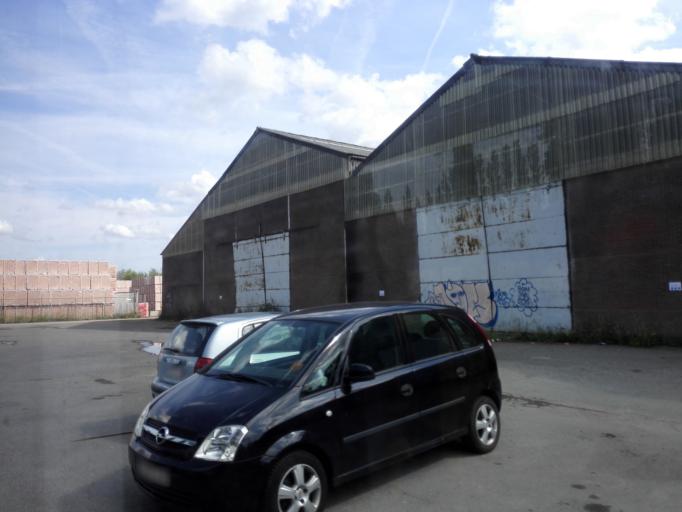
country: BE
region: Flanders
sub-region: Provincie Antwerpen
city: Rumst
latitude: 51.0803
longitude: 4.4058
